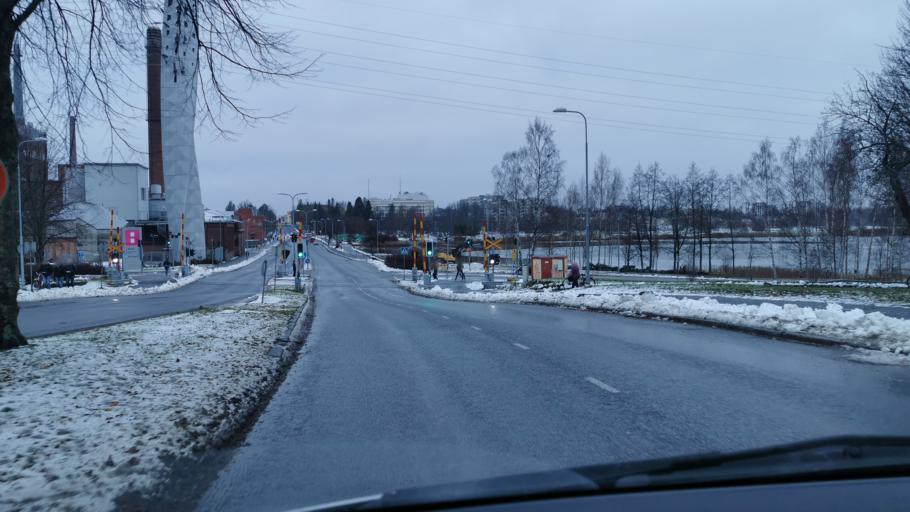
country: FI
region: Ostrobothnia
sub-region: Vaasa
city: Vaasa
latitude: 63.1006
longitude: 21.6051
